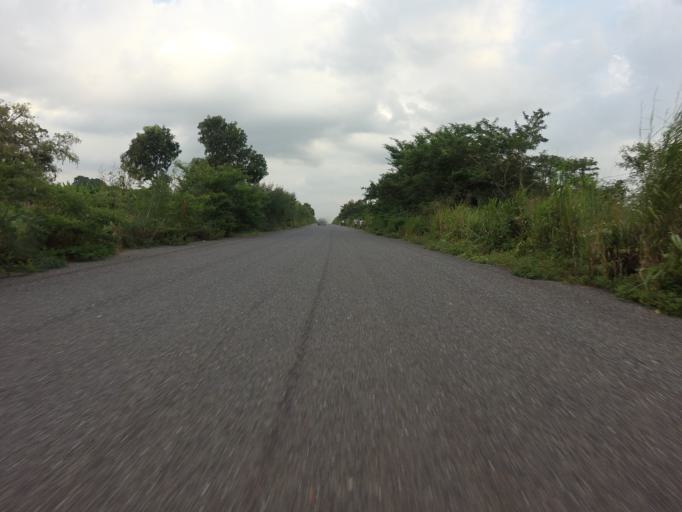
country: GH
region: Volta
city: Ho
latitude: 6.4953
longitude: 0.4870
